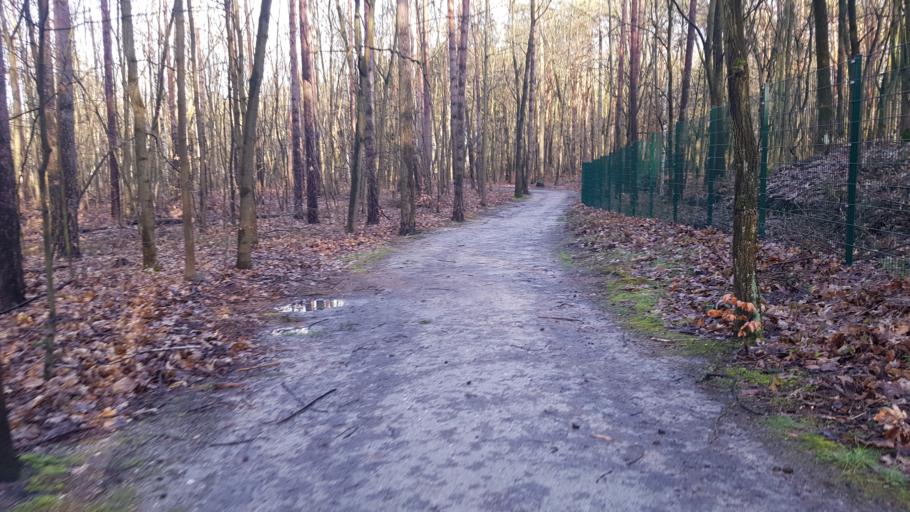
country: DE
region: Brandenburg
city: Finsterwalde
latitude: 51.6310
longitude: 13.6877
